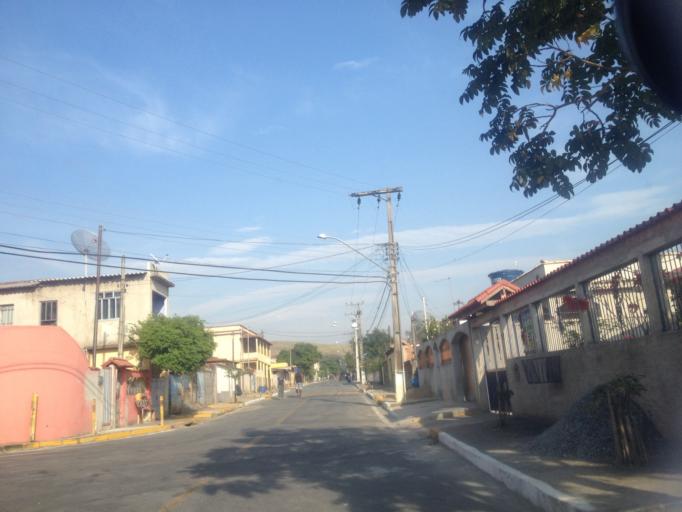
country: BR
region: Rio de Janeiro
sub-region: Porto Real
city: Porto Real
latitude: -22.4480
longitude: -44.3053
